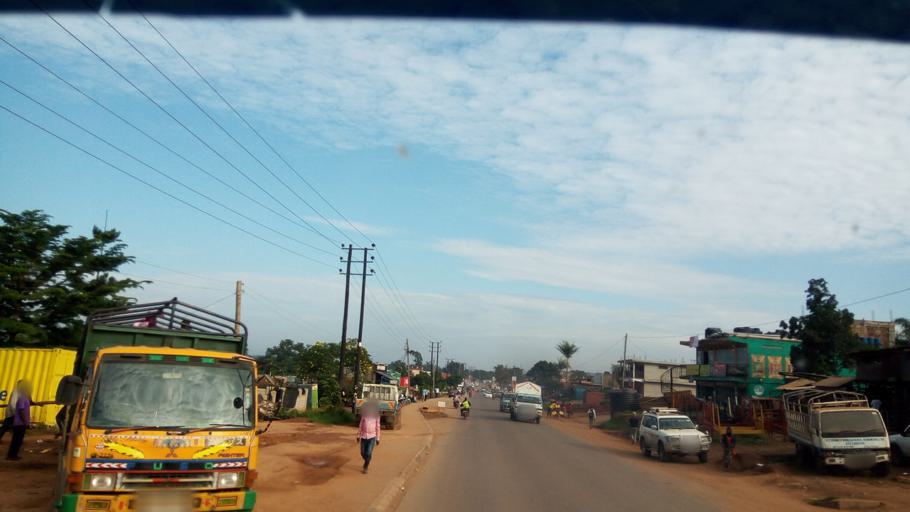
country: UG
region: Central Region
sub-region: Wakiso District
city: Wakiso
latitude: 0.4632
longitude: 32.5244
